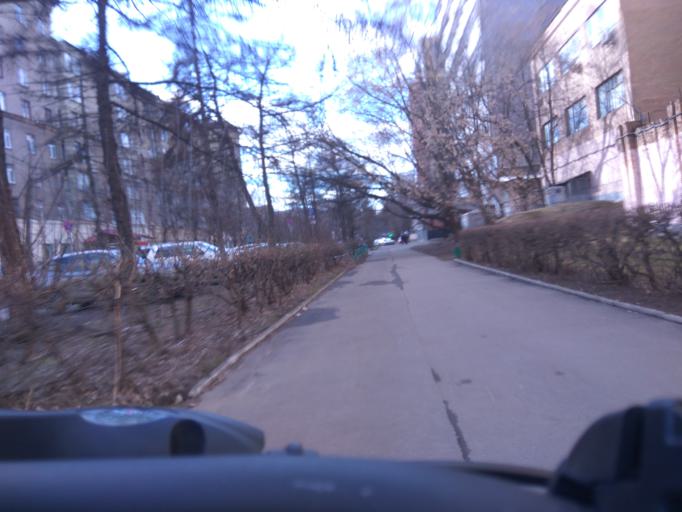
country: RU
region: Moscow
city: Sokol'niki
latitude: 55.8043
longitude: 37.6471
